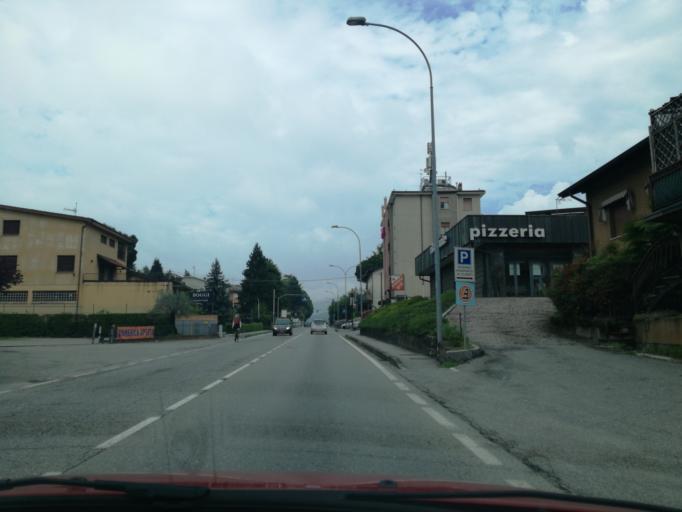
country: IT
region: Lombardy
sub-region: Provincia di Lecco
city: Canova-San Zeno
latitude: 45.7082
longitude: 9.4085
